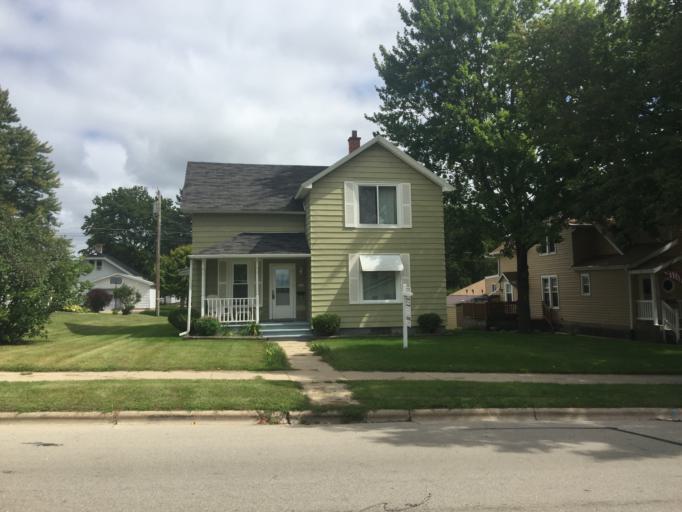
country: US
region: Wisconsin
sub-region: Oconto County
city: Oconto Falls
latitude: 44.8721
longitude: -88.1409
